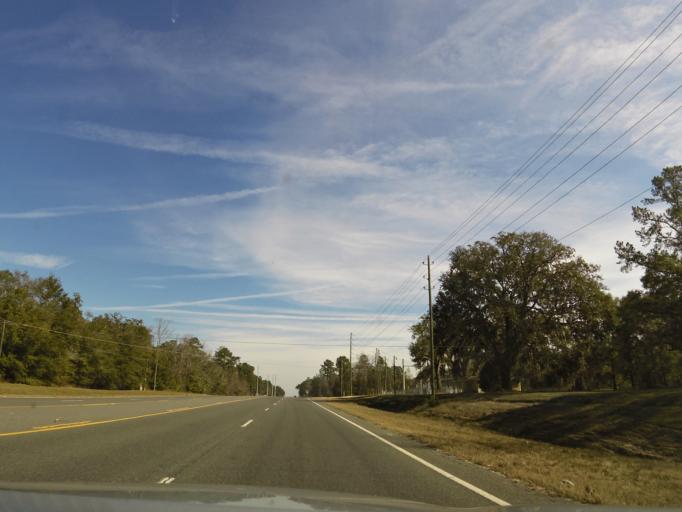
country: US
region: Georgia
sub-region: Brantley County
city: Nahunta
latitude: 31.2303
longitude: -81.7773
